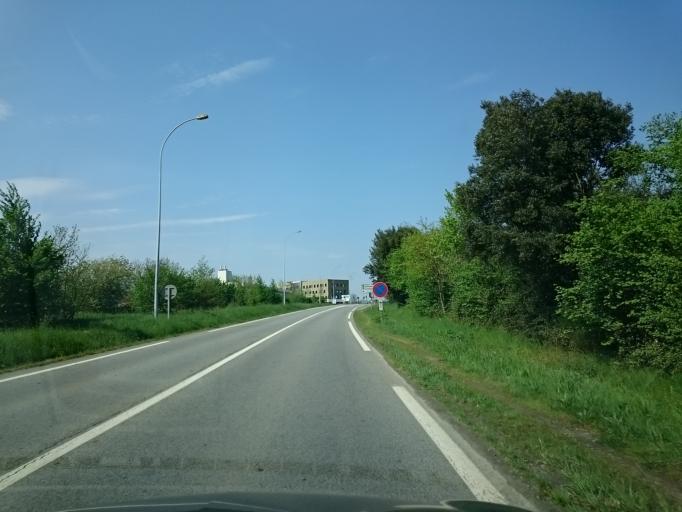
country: FR
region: Brittany
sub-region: Departement d'Ille-et-Vilaine
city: Chantepie
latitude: 48.0859
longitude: -1.6242
